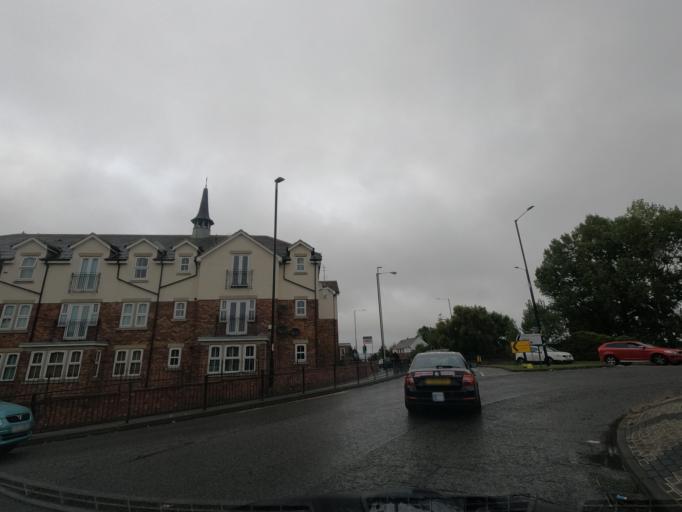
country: GB
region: England
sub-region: Middlesbrough
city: Nunthorpe
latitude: 54.5501
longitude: -1.1801
